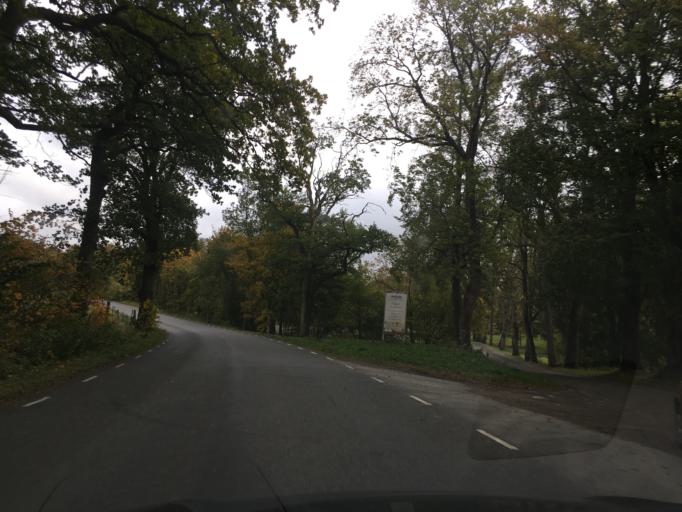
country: SE
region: Skane
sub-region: Tomelilla Kommun
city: Tomelilla
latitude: 55.6442
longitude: 14.0438
